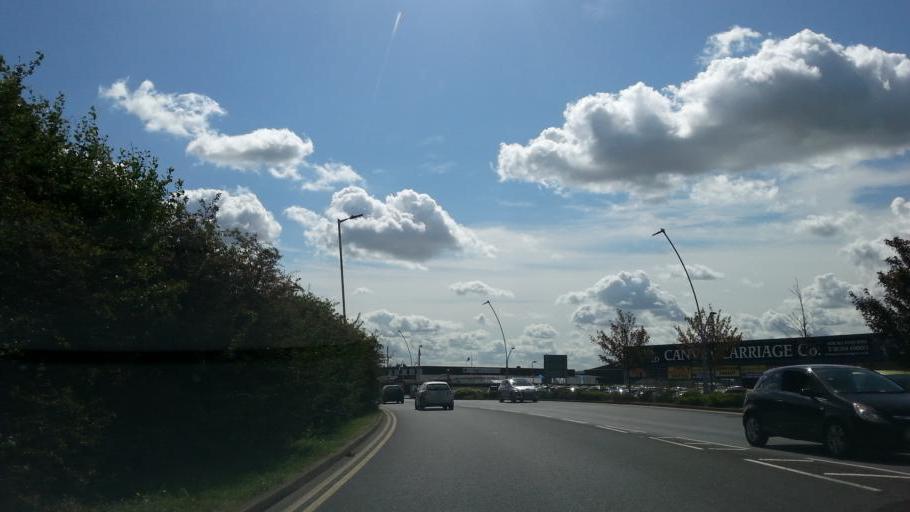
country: GB
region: England
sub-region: Essex
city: Canvey Island
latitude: 51.5234
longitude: 0.5572
